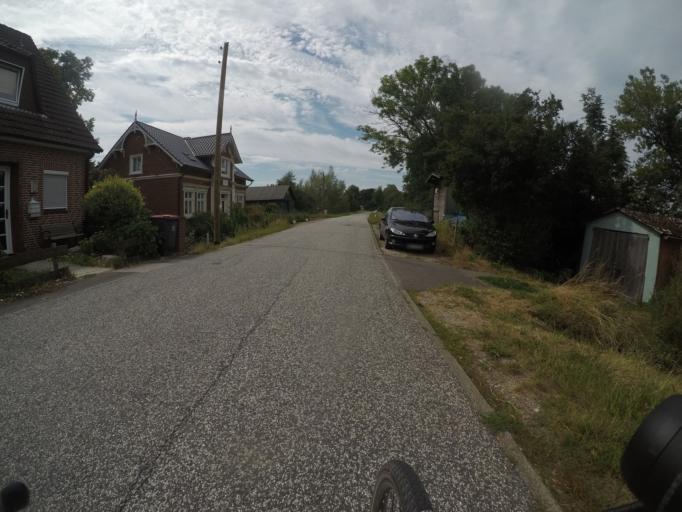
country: DE
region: Hamburg
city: Bergedorf
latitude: 53.4635
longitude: 10.1768
